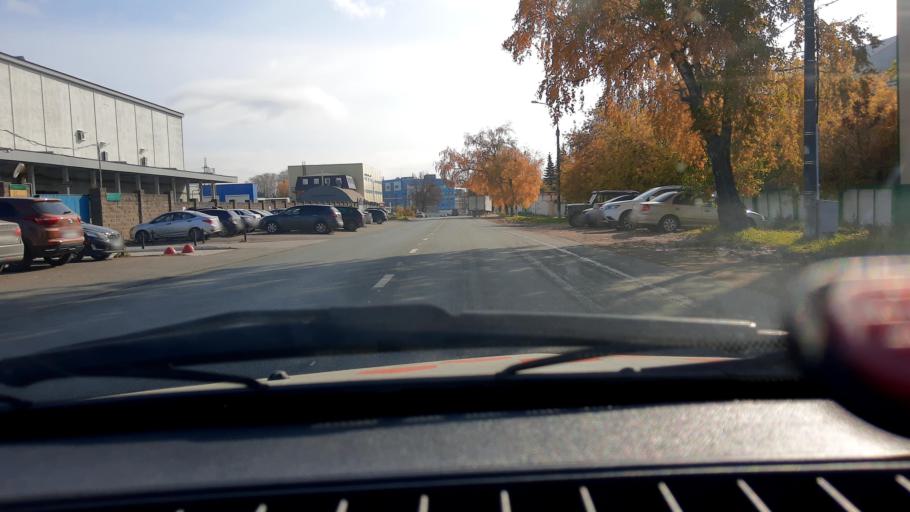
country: RU
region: Bashkortostan
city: Ufa
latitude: 54.8012
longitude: 56.1054
